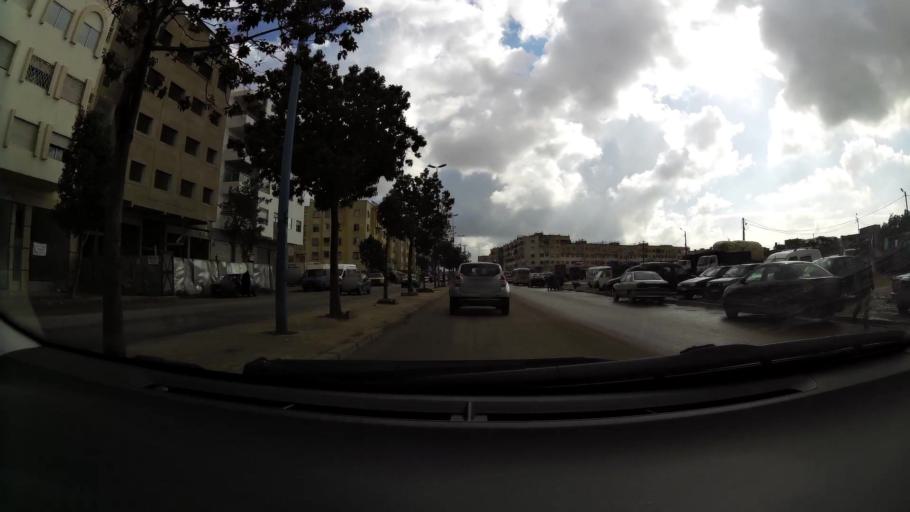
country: MA
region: Grand Casablanca
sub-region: Mediouna
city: Tit Mellil
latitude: 33.5898
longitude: -7.5196
